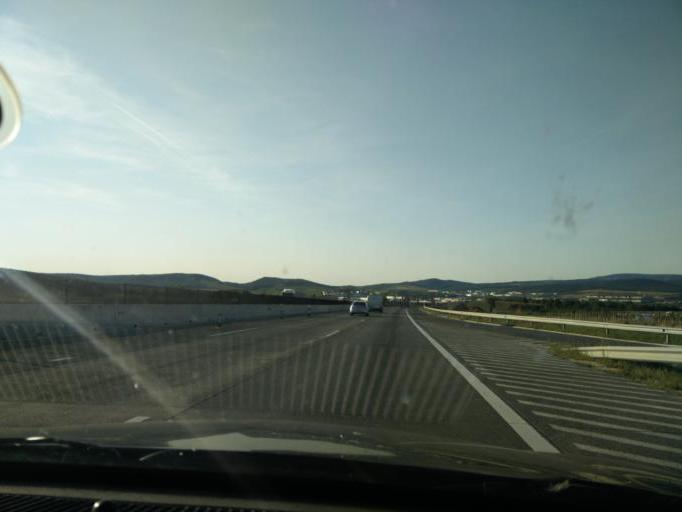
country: HU
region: Pest
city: Toeroekbalint
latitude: 47.4299
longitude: 18.8970
